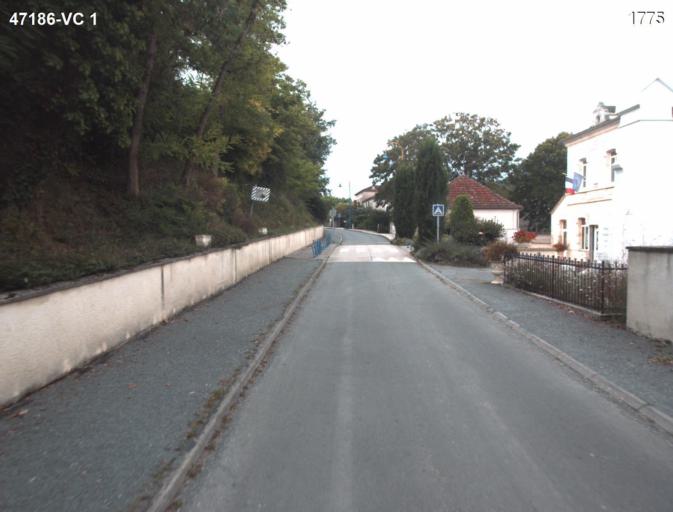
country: FR
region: Aquitaine
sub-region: Departement du Lot-et-Garonne
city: Port-Sainte-Marie
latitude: 44.2030
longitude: 0.4382
